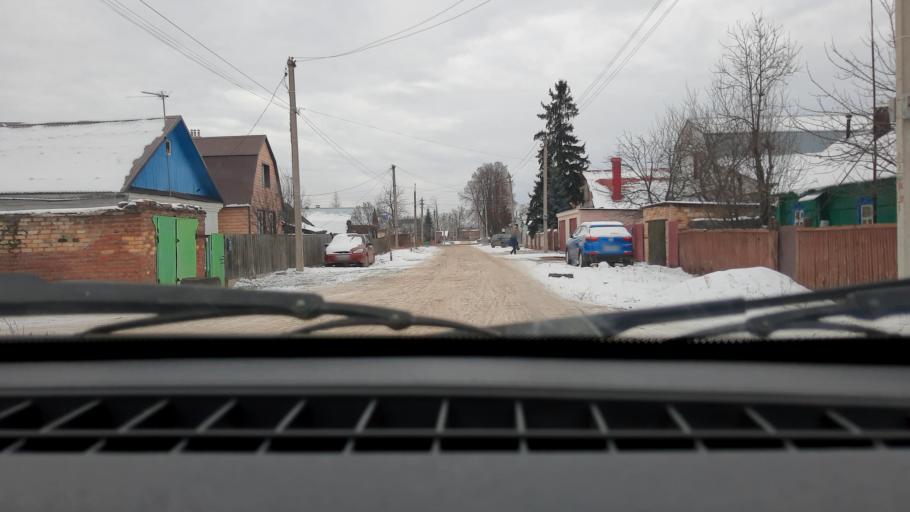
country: RU
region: Bashkortostan
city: Iglino
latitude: 54.7640
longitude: 56.2268
